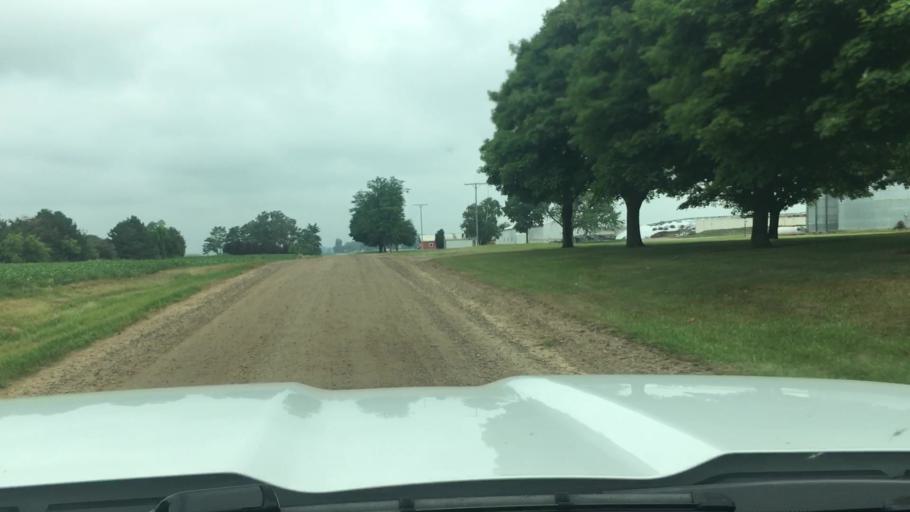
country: US
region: Michigan
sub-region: Sanilac County
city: Marlette
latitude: 43.3466
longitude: -82.9754
